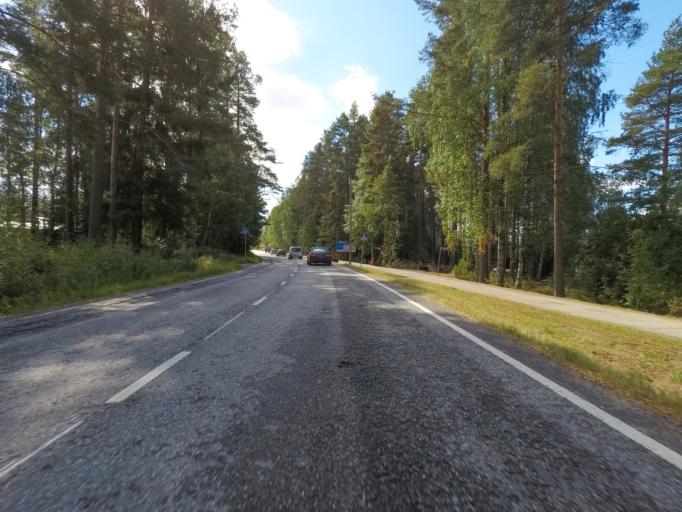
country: FI
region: Central Finland
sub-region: Jyvaeskylae
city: Toivakka
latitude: 62.1009
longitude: 26.0848
